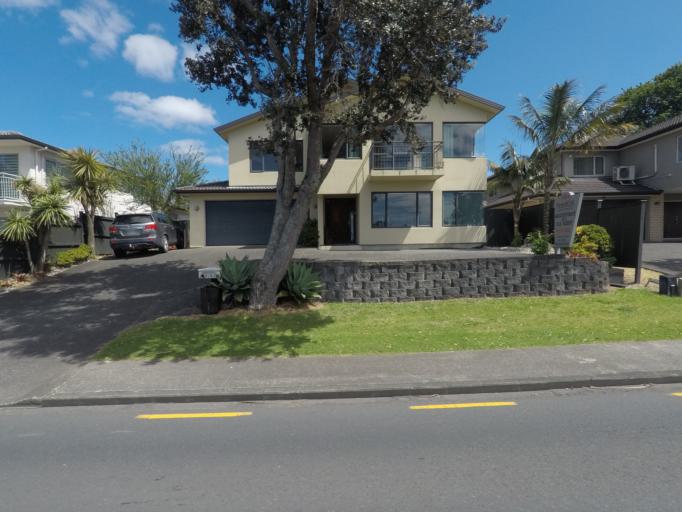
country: NZ
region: Auckland
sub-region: Auckland
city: Rosebank
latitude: -36.8504
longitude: 174.6511
